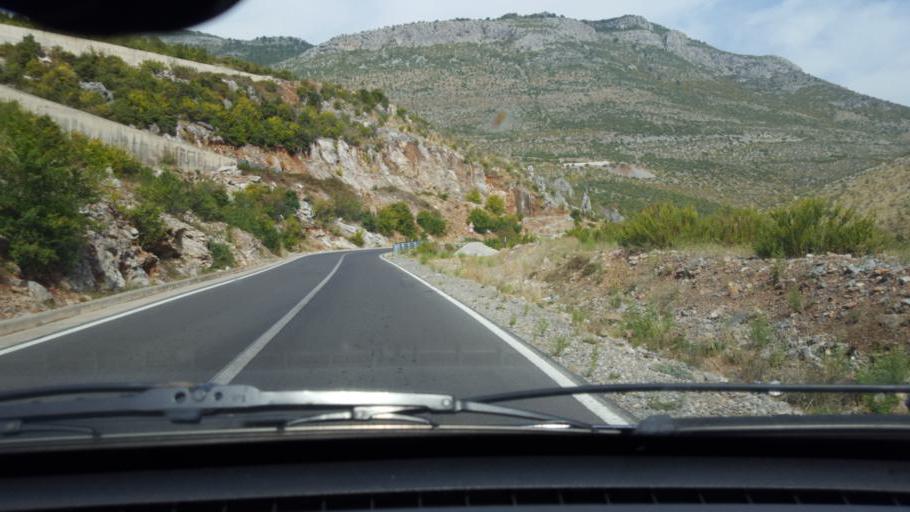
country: AL
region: Shkoder
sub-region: Rrethi i Malesia e Madhe
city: Hot
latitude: 42.3679
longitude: 19.4488
